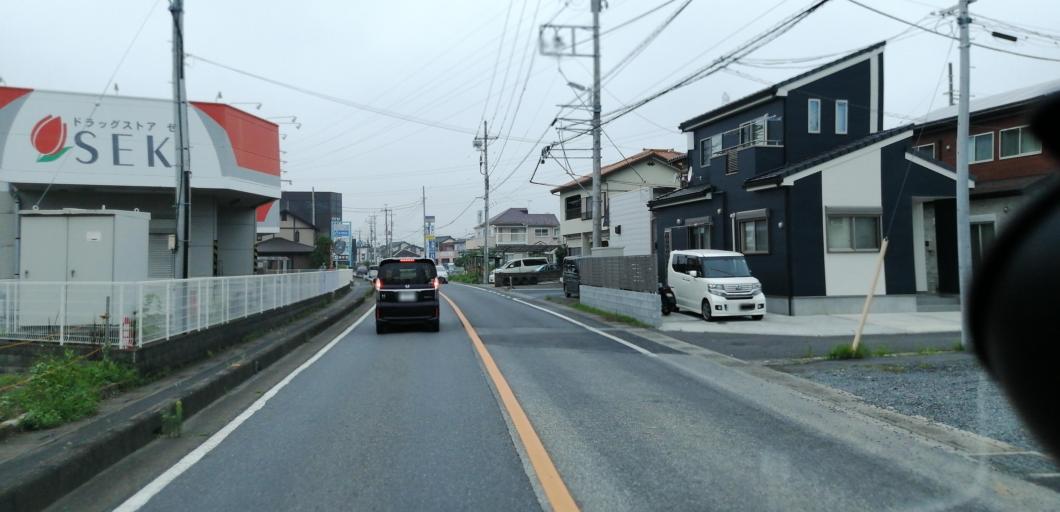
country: JP
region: Saitama
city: Kukichuo
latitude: 36.1009
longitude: 139.6655
